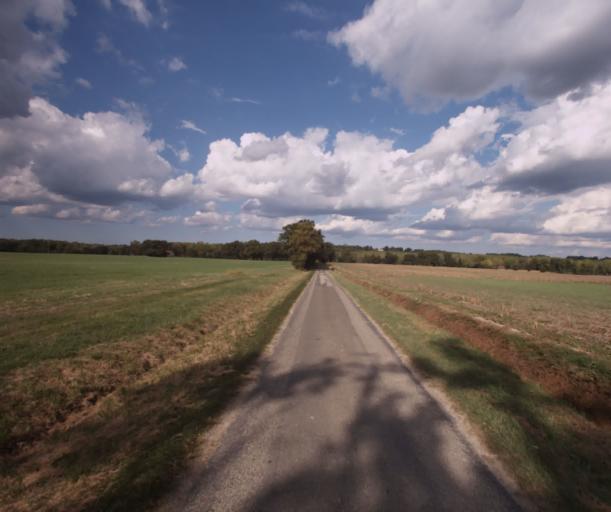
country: FR
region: Midi-Pyrenees
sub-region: Departement du Gers
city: Cazaubon
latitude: 43.9083
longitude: -0.0542
